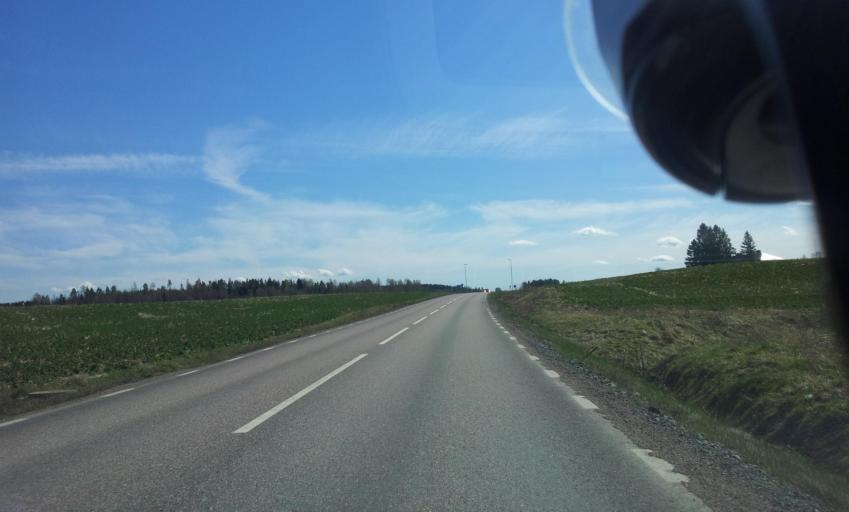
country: SE
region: Dalarna
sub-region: Borlange Kommun
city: Ornas
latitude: 60.4789
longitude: 15.4947
